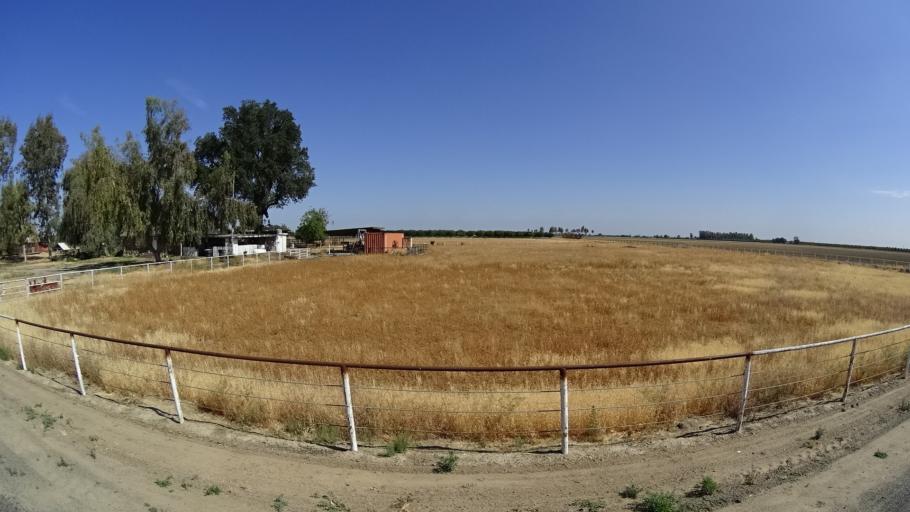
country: US
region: California
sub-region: Kings County
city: Armona
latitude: 36.2547
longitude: -119.7184
